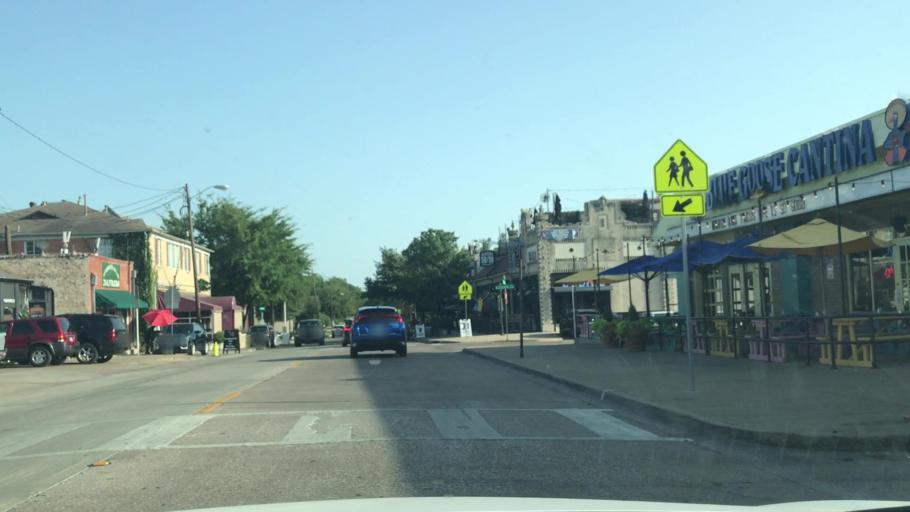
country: US
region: Texas
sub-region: Dallas County
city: Highland Park
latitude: 32.8239
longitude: -96.7702
